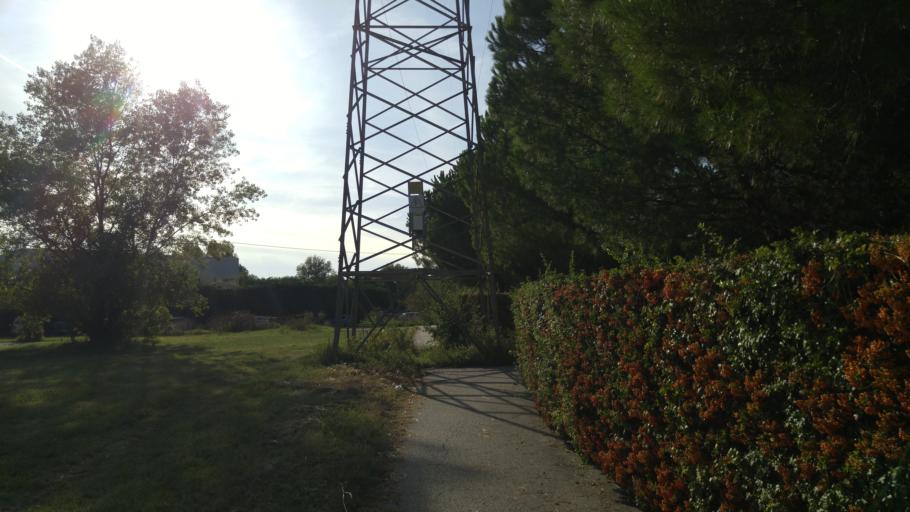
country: IT
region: The Marches
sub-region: Provincia di Pesaro e Urbino
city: Fano
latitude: 43.8347
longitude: 13.0194
